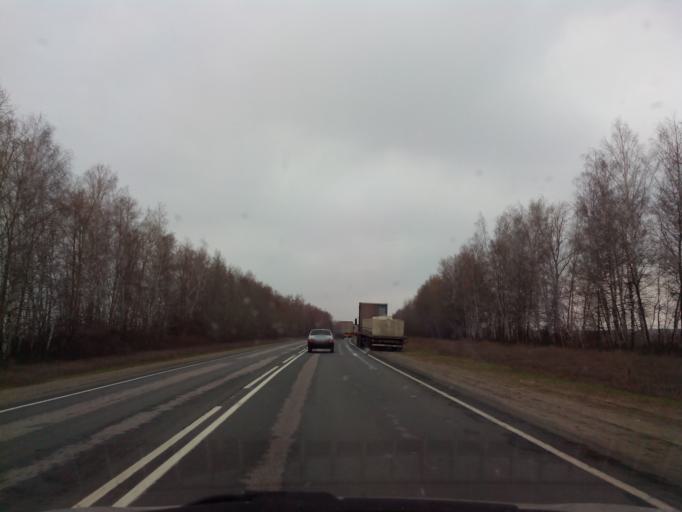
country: RU
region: Tambov
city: Pervomayskiy
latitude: 53.0963
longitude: 40.3960
